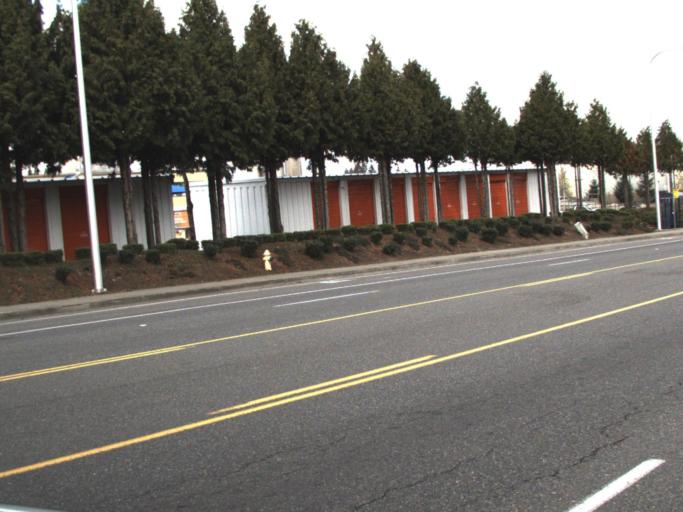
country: US
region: Washington
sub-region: King County
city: Lakeland South
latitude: 47.2851
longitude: -122.3136
